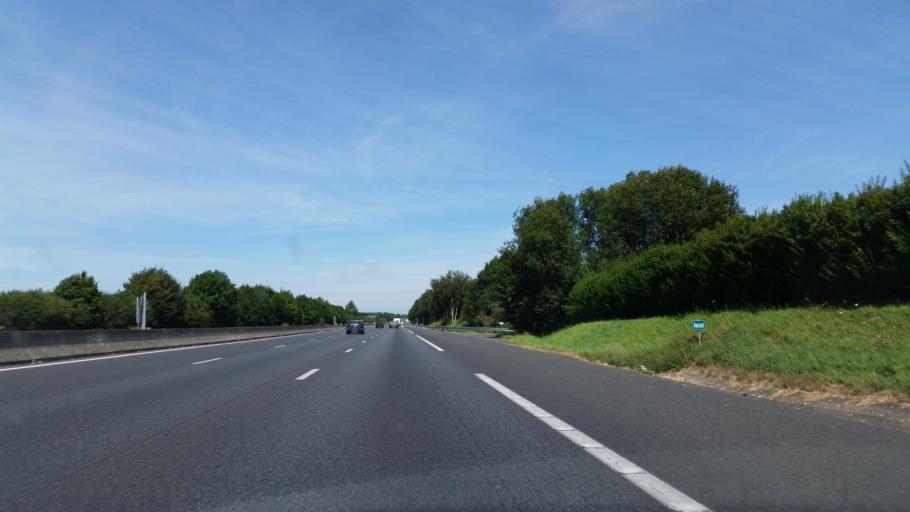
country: FR
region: Nord-Pas-de-Calais
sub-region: Departement du Pas-de-Calais
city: Bapaume
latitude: 50.1262
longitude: 2.8718
